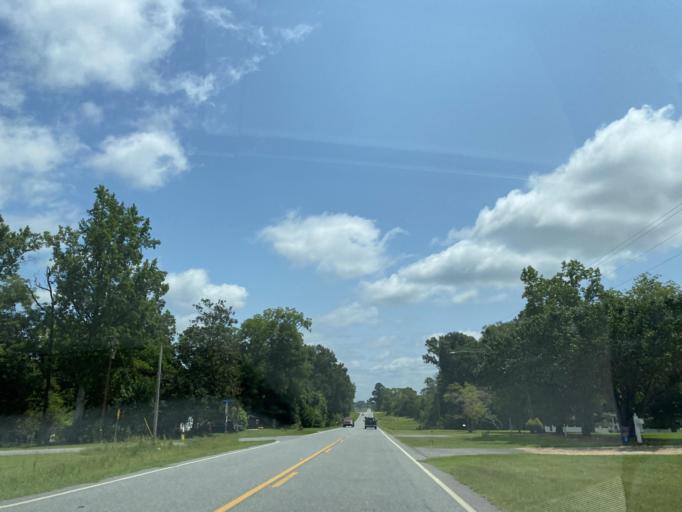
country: US
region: Georgia
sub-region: Telfair County
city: Helena
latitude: 32.0190
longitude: -83.0514
